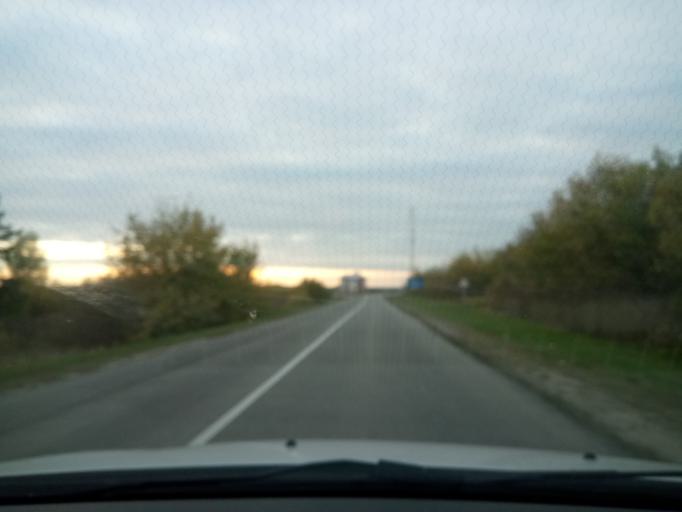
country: RU
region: Nizjnij Novgorod
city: Buturlino
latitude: 55.5966
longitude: 44.8862
